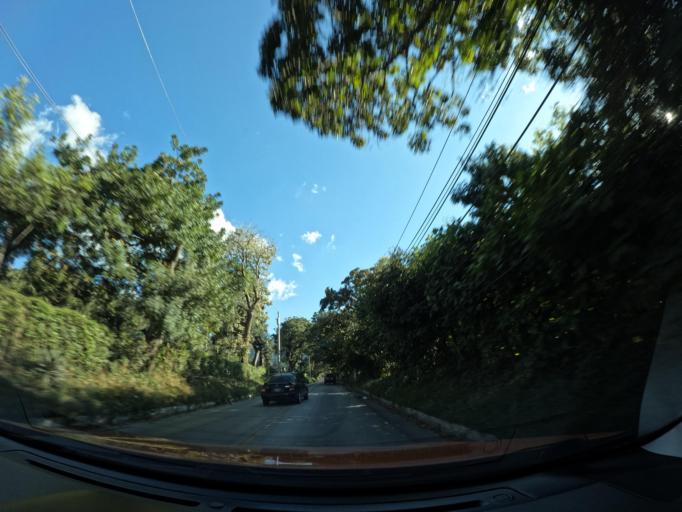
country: GT
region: Sacatepequez
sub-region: Municipio de Santa Maria de Jesus
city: Santa Maria de Jesus
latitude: 14.5277
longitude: -90.7265
